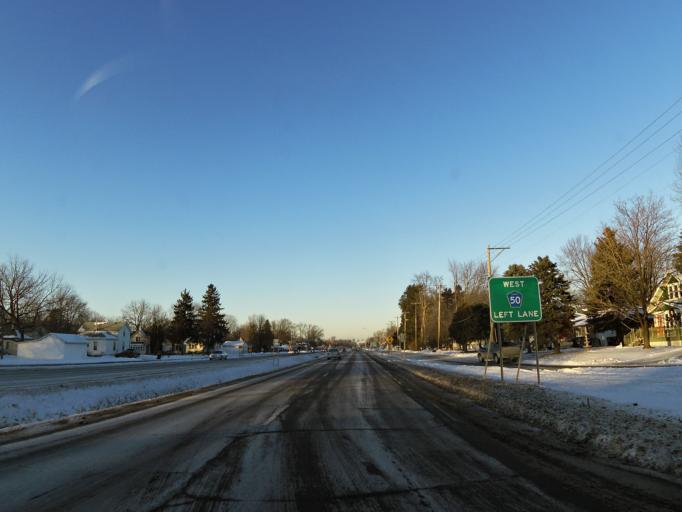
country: US
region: Minnesota
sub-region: Dakota County
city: Farmington
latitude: 44.6380
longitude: -93.1369
